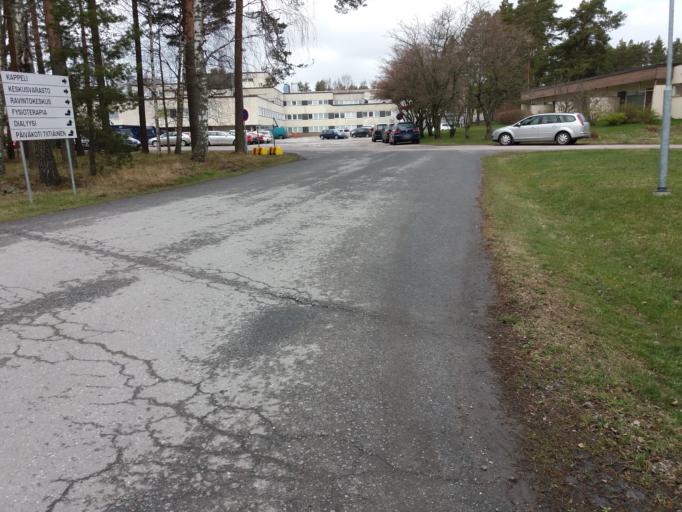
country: FI
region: Varsinais-Suomi
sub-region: Vakka-Suomi
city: Uusikaupunki
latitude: 60.7950
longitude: 21.4254
